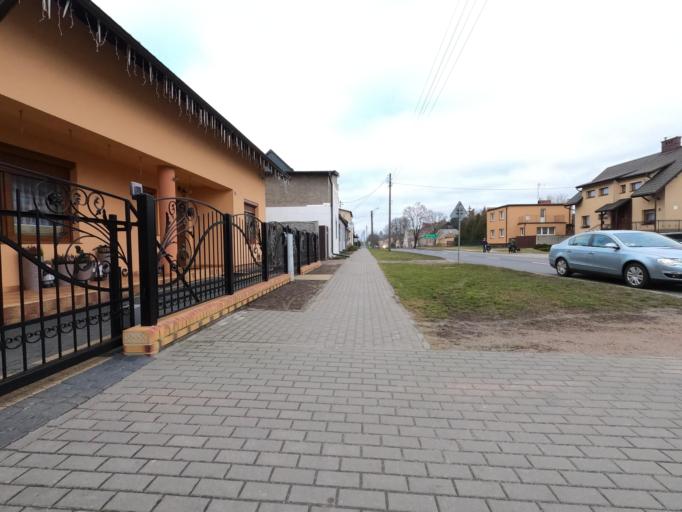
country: PL
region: Greater Poland Voivodeship
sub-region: Powiat pilski
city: Bialosliwie
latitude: 53.1063
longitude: 17.1256
